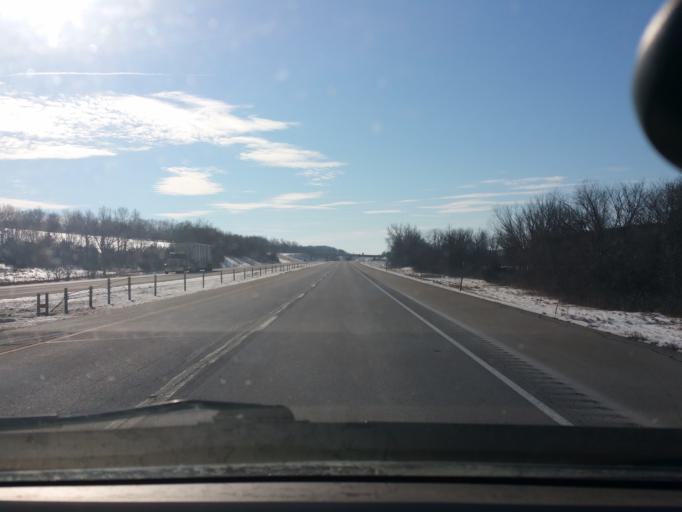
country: US
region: Iowa
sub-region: Clarke County
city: Osceola
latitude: 41.0766
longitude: -93.7813
